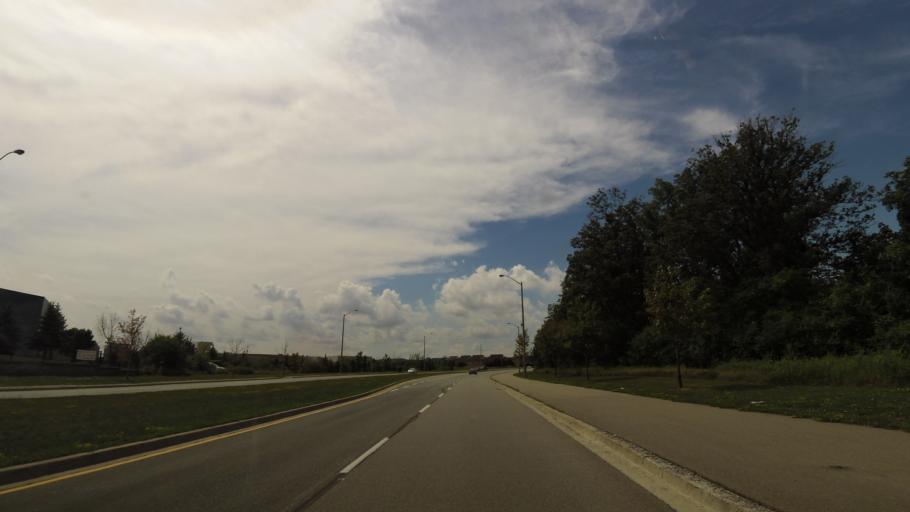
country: CA
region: Ontario
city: Brampton
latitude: 43.7640
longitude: -79.7063
